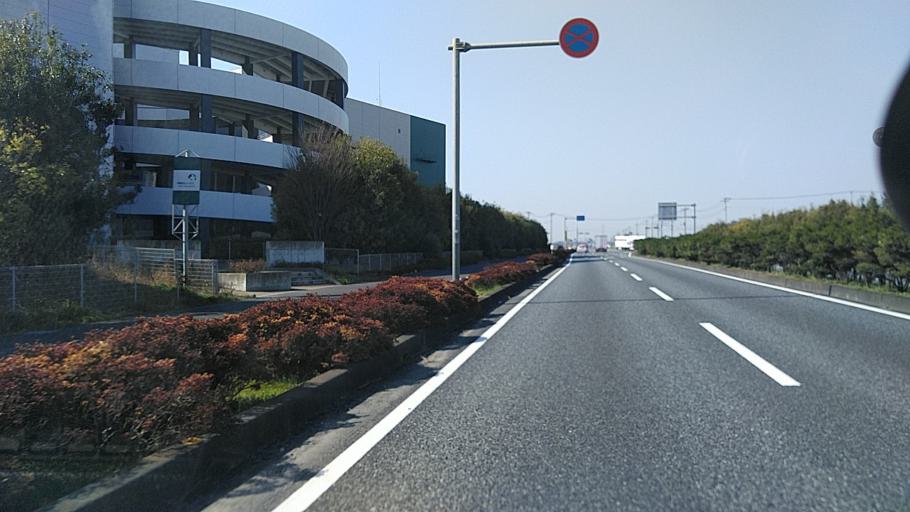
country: JP
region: Saitama
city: Sakado
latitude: 35.9868
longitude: 139.4608
